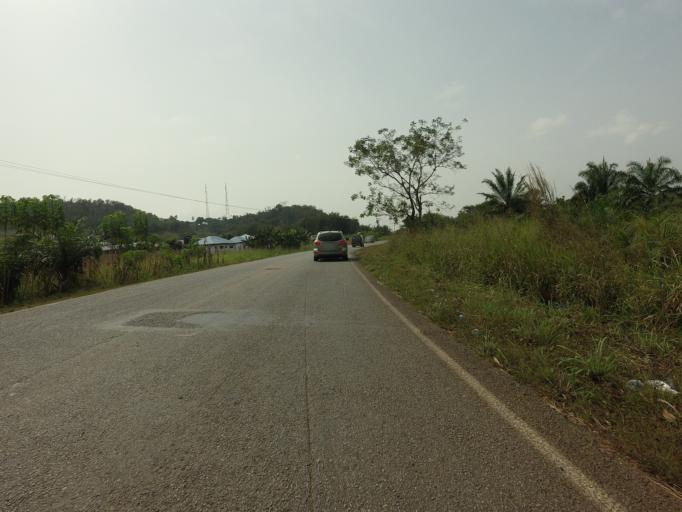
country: GH
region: Volta
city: Ho
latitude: 6.3460
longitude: 0.1748
